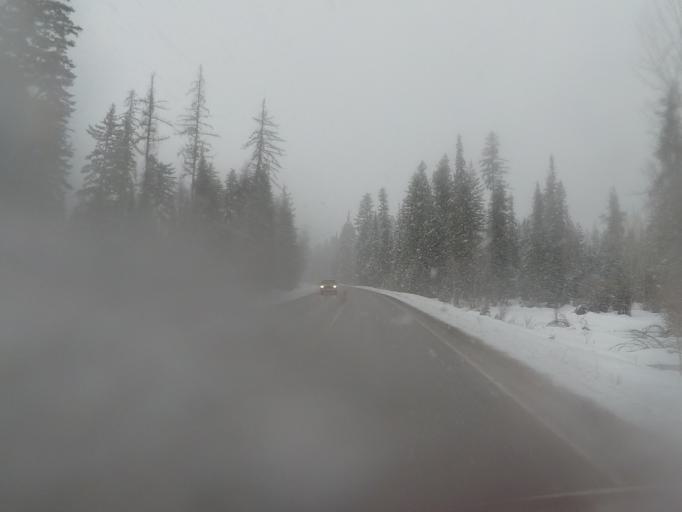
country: US
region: Montana
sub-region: Missoula County
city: Seeley Lake
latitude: 47.4360
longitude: -113.6697
